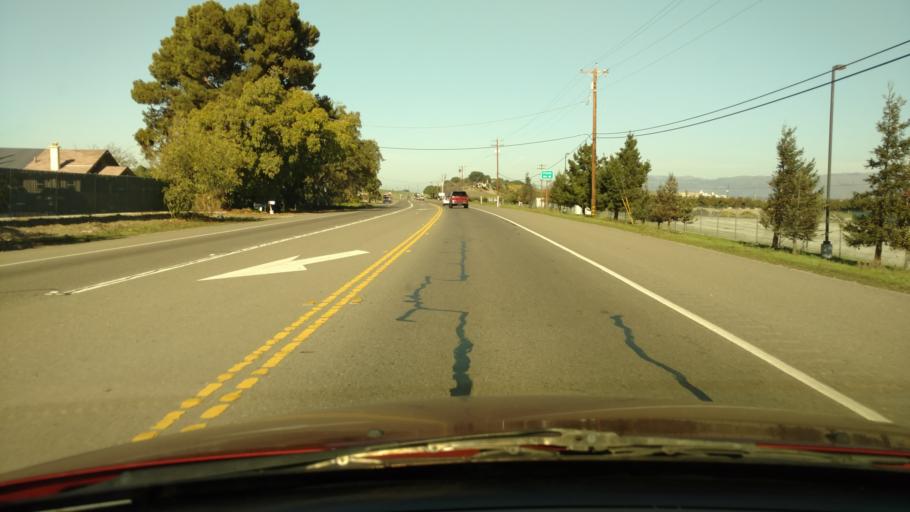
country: US
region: California
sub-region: San Benito County
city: Hollister
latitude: 36.8806
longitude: -121.4141
